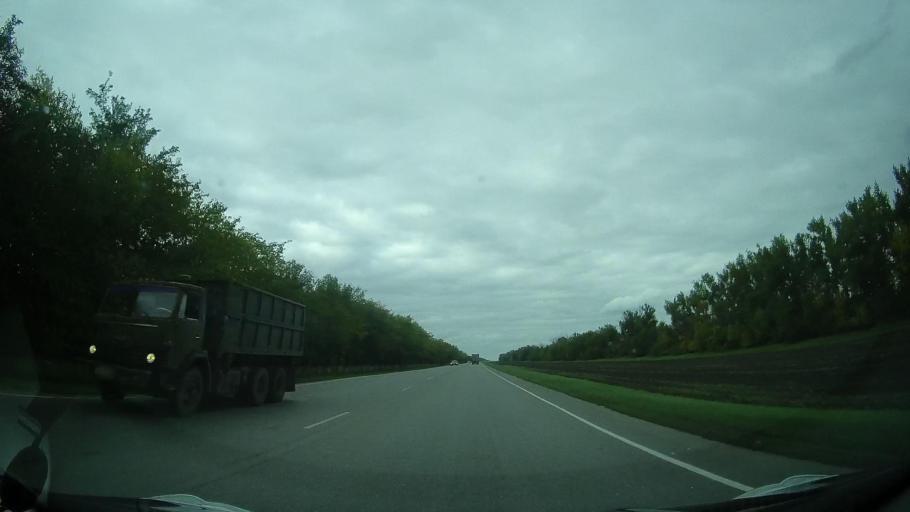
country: RU
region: Rostov
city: Yegorlykskaya
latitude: 46.6161
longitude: 40.6020
